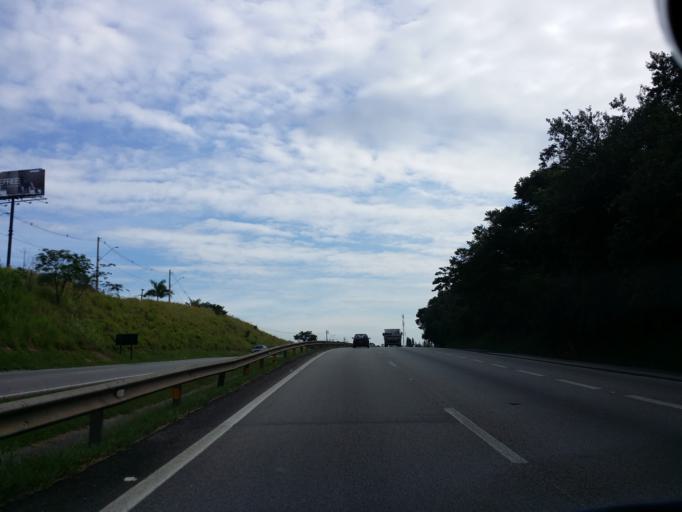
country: BR
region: Sao Paulo
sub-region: Itupeva
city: Itupeva
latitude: -23.1983
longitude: -46.9977
